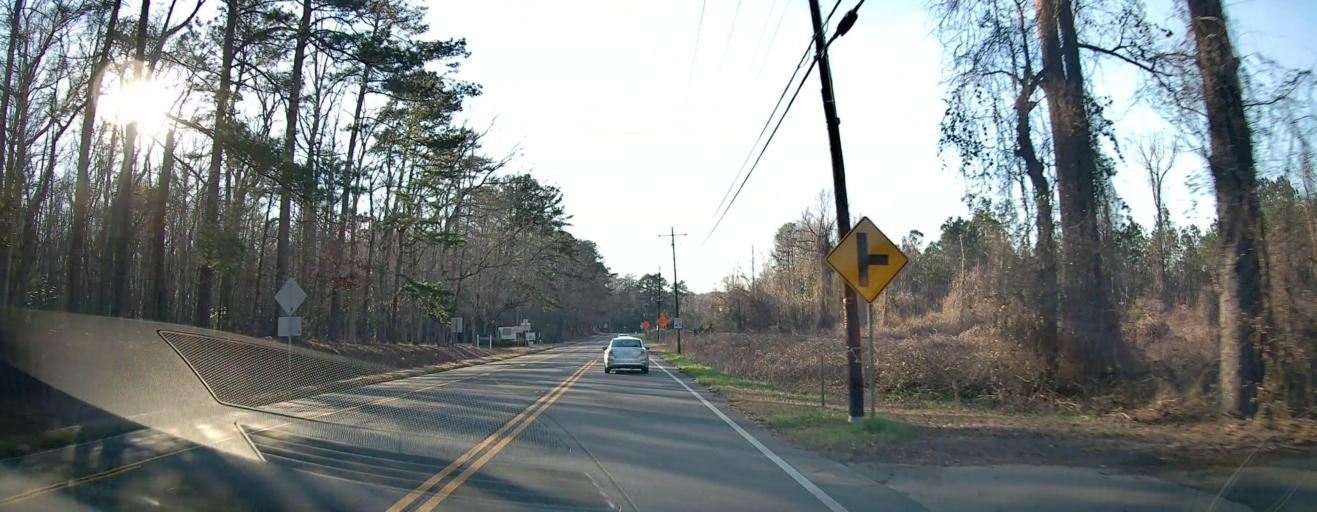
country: US
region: Georgia
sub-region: Meriwether County
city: Manchester
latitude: 32.8911
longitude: -84.6842
